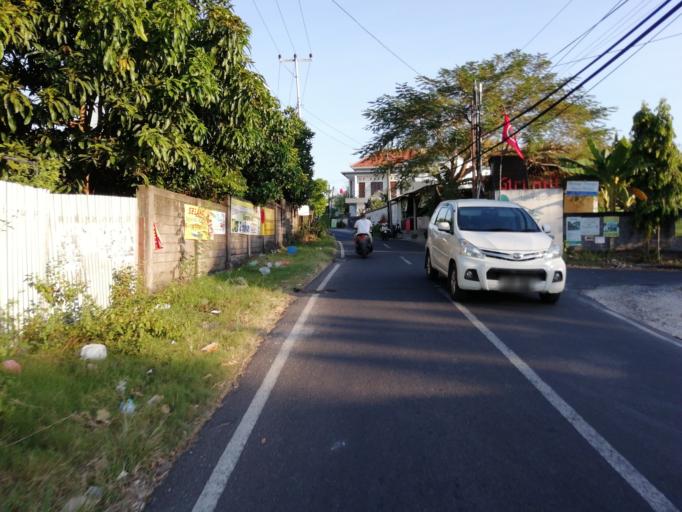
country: ID
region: Bali
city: Bualu
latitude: -8.7952
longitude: 115.1928
